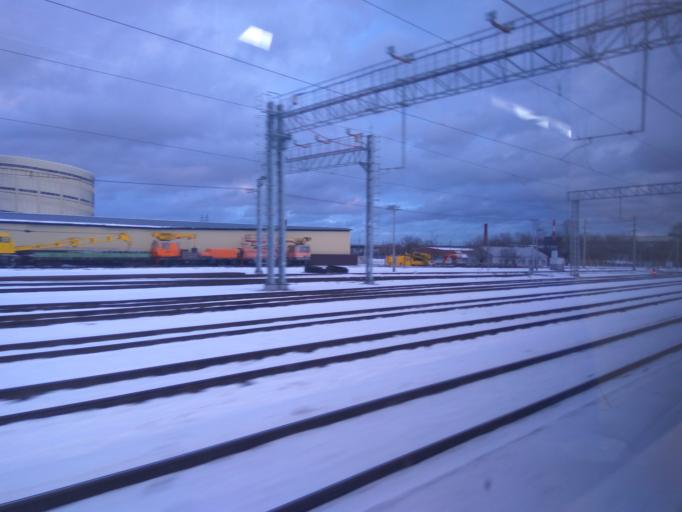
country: RU
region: Moscow
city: Rostokino
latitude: 55.8422
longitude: 37.6592
